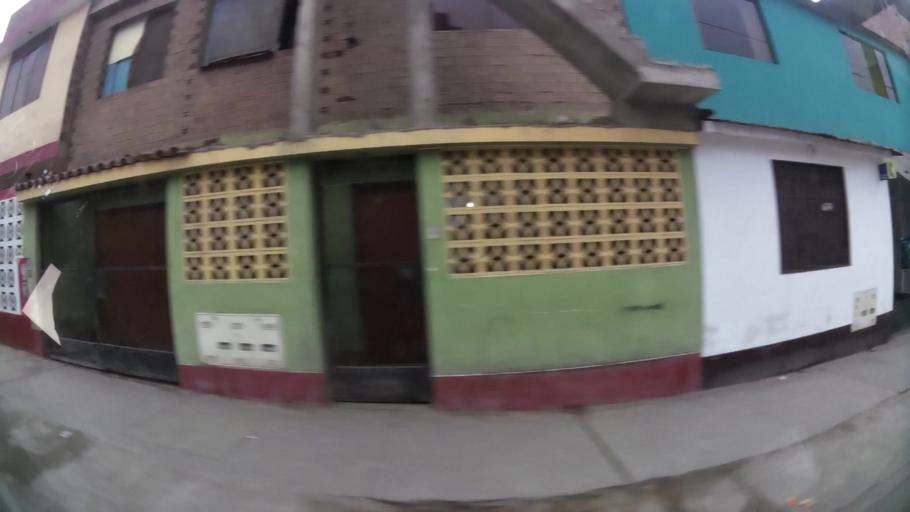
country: PE
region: Lima
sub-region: Lima
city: Surco
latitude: -12.1460
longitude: -76.9776
